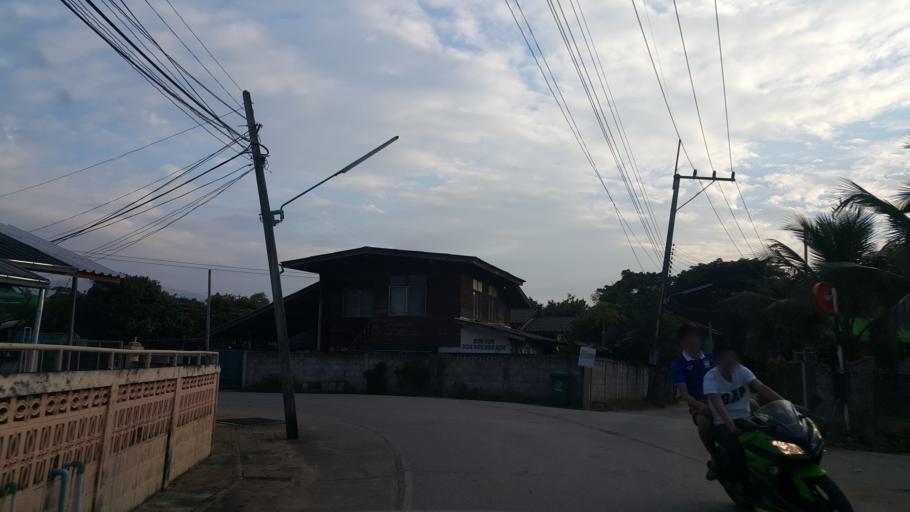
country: TH
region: Lampang
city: Sop Prap
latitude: 17.8735
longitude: 99.3323
